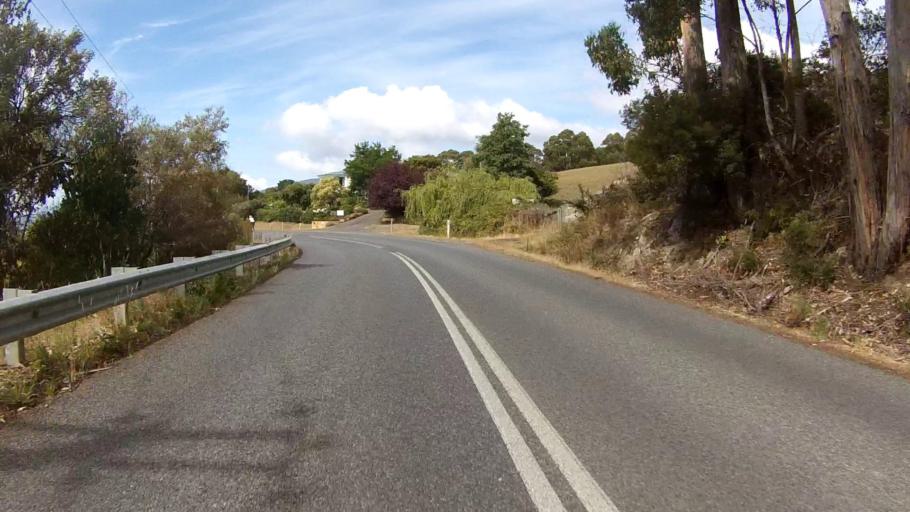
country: AU
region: Tasmania
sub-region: Kingborough
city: Kettering
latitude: -43.1413
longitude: 147.2434
